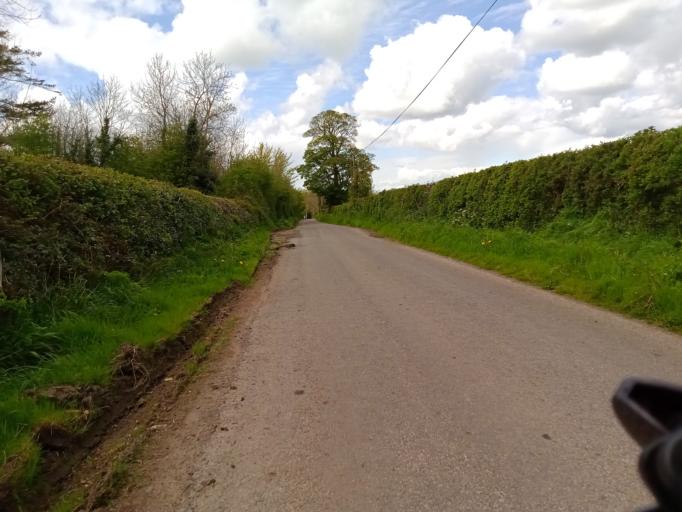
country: IE
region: Leinster
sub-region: Kilkenny
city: Thomastown
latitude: 52.5811
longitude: -7.1304
